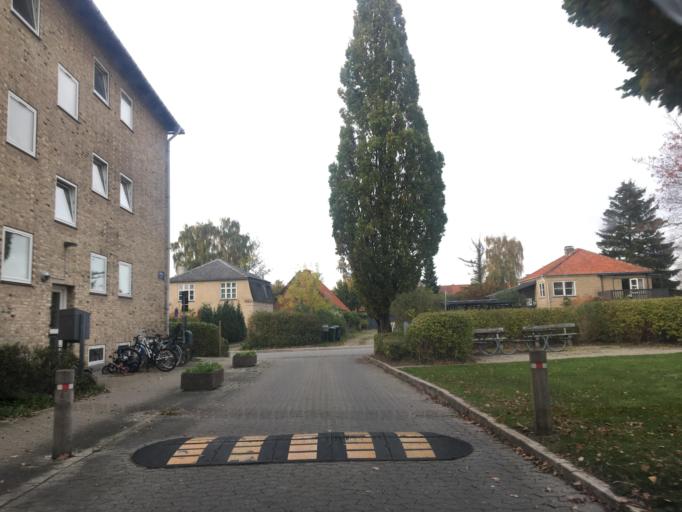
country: DK
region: Capital Region
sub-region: Herlev Kommune
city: Herlev
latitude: 55.7185
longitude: 12.4623
